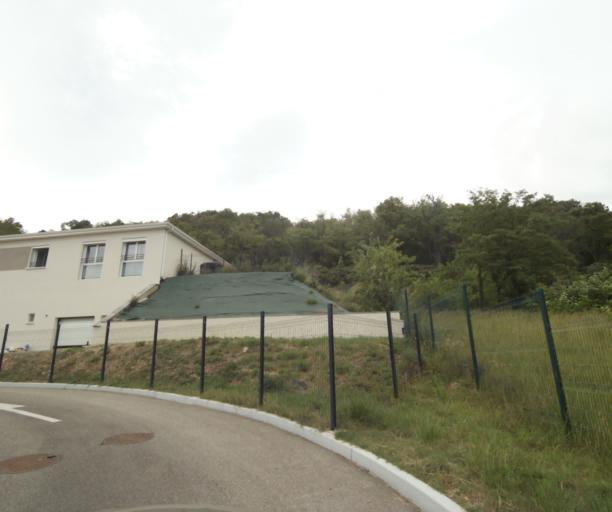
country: FR
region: Rhone-Alpes
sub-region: Departement de l'Ain
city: Miribel
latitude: 45.8303
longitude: 4.9621
